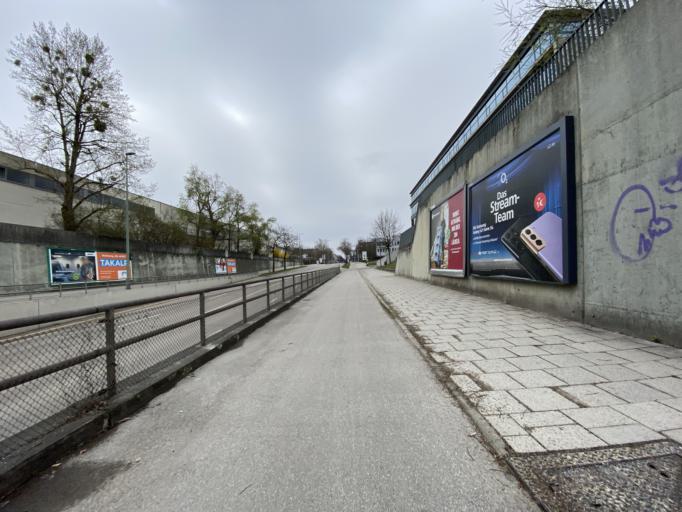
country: DE
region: Bavaria
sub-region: Upper Bavaria
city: Munich
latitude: 48.1902
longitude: 11.5724
